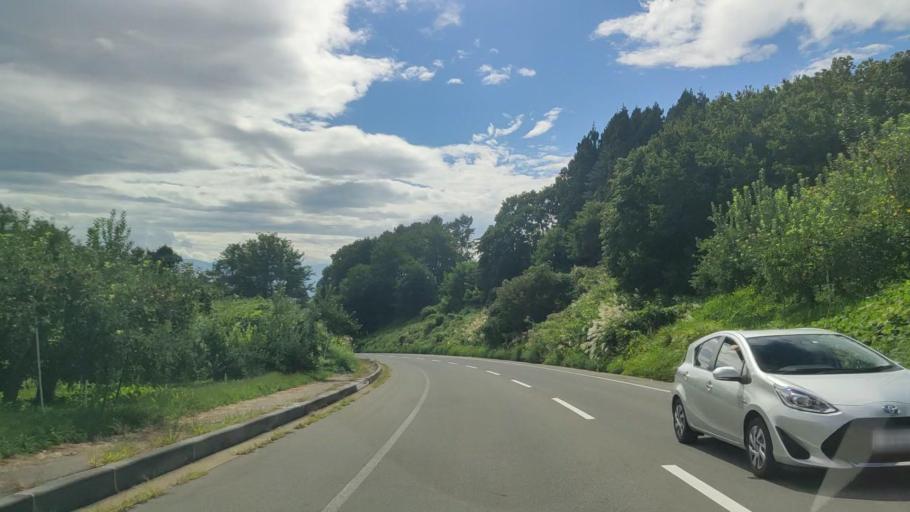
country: JP
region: Nagano
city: Nakano
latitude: 36.7957
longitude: 138.3142
